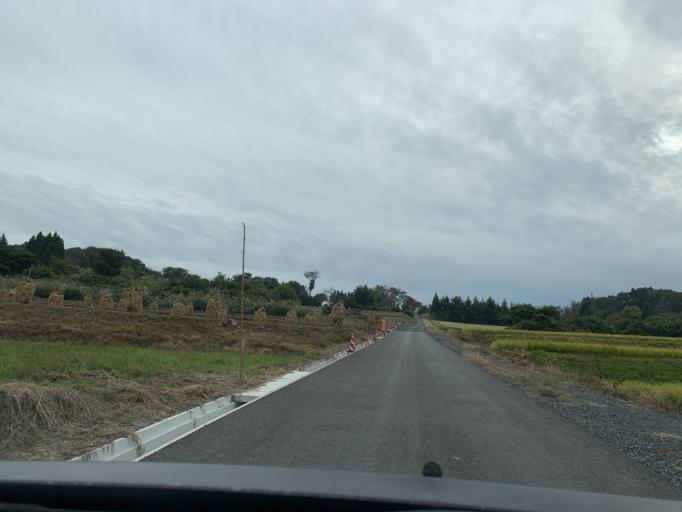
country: JP
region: Iwate
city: Ichinoseki
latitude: 38.9529
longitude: 141.1142
